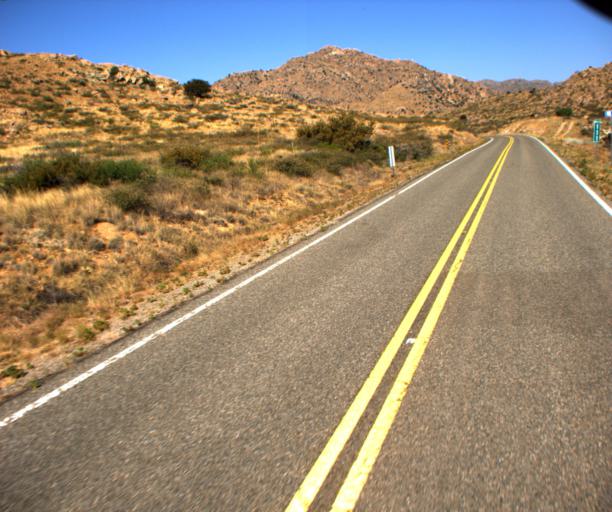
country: US
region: Arizona
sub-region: Graham County
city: Swift Trail Junction
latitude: 32.5611
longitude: -109.7777
